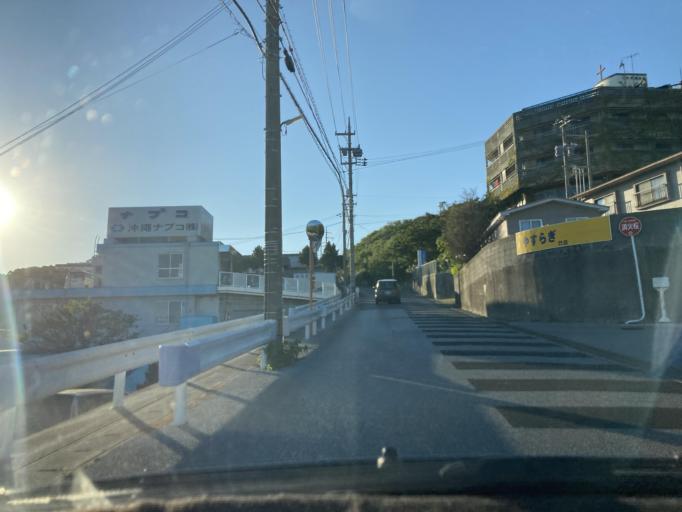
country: JP
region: Okinawa
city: Naha-shi
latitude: 26.2105
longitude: 127.7328
